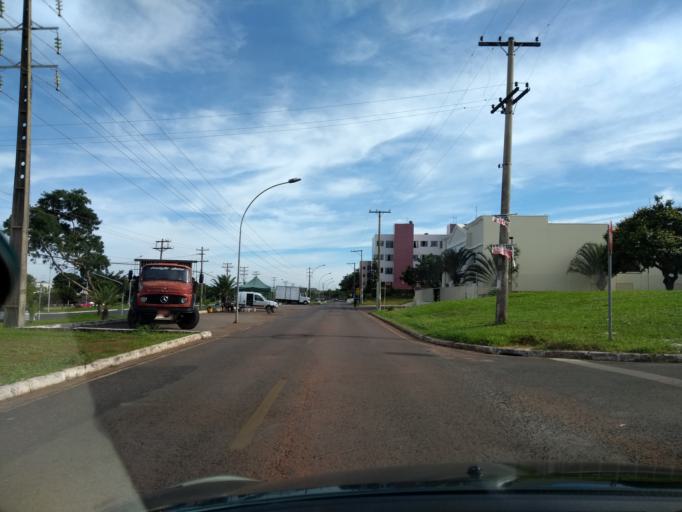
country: BR
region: Federal District
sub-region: Brasilia
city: Brasilia
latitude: -15.7857
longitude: -47.9307
